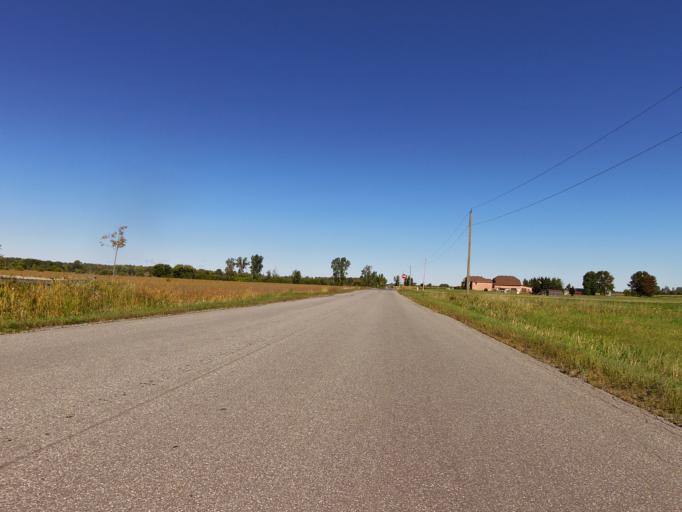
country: CA
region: Ontario
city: Clarence-Rockland
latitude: 45.3179
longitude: -75.4101
